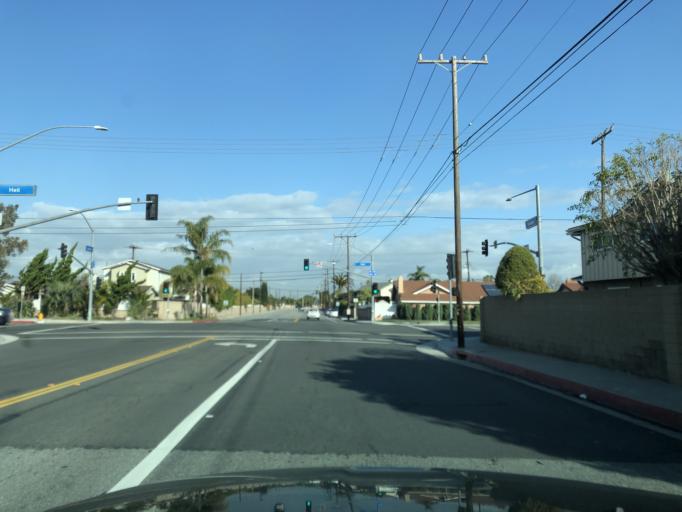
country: US
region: California
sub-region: Orange County
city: Westminster
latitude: 33.7221
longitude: -118.0327
